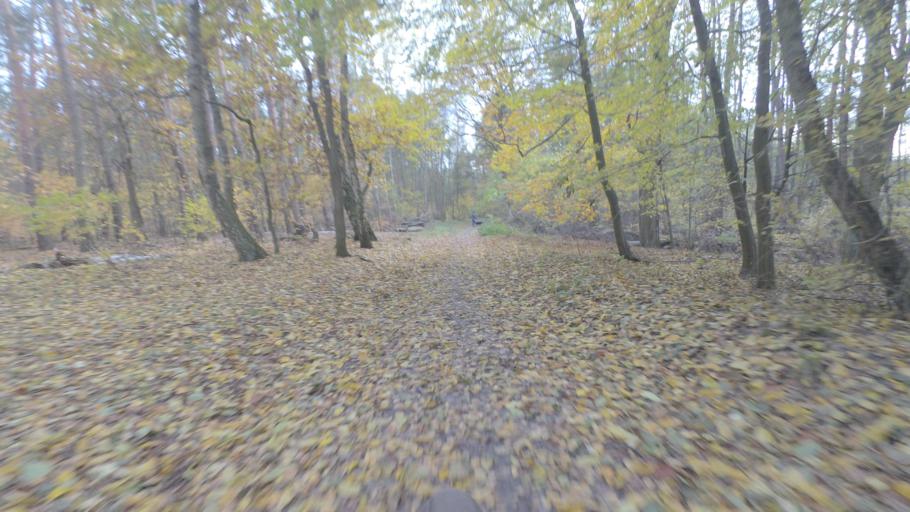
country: DE
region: Brandenburg
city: Rangsdorf
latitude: 52.3170
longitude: 13.4164
